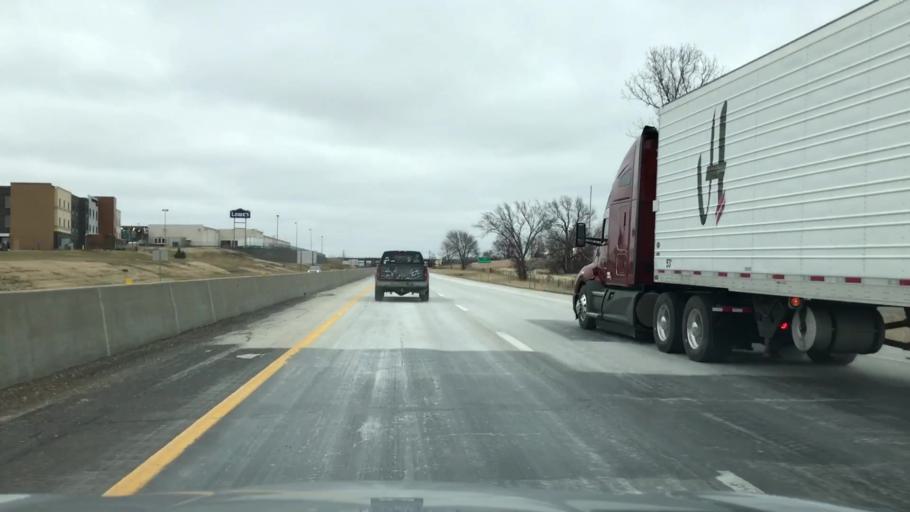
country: US
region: Missouri
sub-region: Livingston County
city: Chillicothe
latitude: 39.7732
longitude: -93.5478
